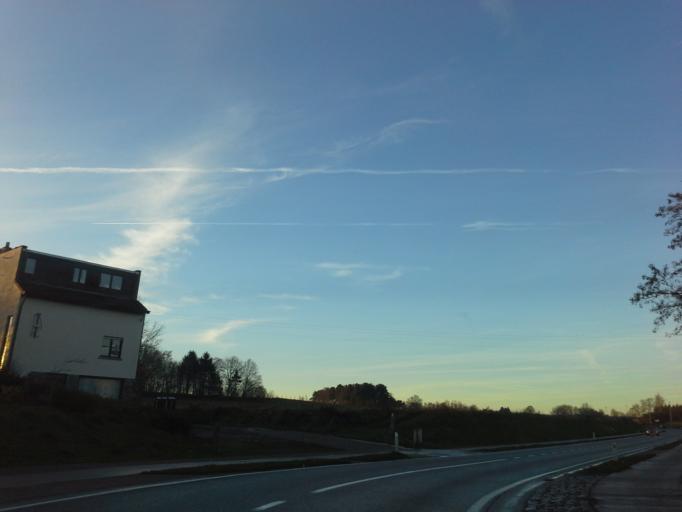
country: BE
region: Flanders
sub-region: Provincie Vlaams-Brabant
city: Scherpenheuvel-Zichem
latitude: 50.9992
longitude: 4.9778
